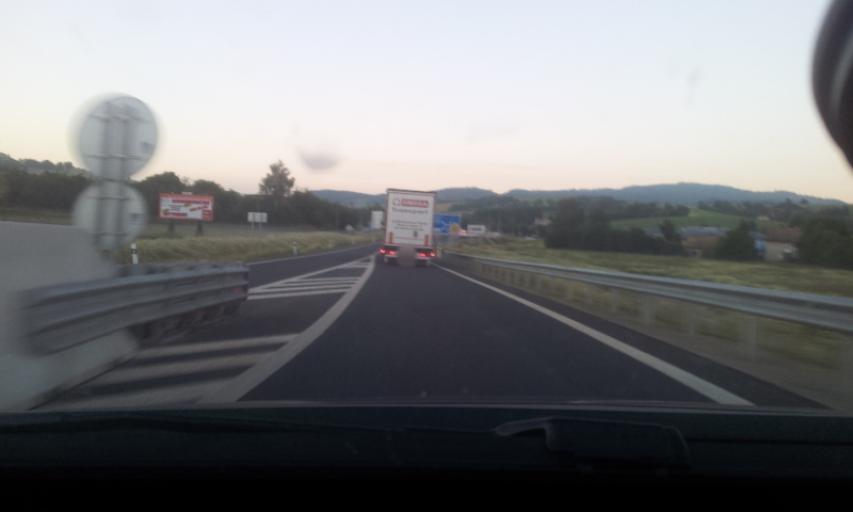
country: SK
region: Banskobystricky
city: Detva
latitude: 48.5313
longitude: 19.4543
